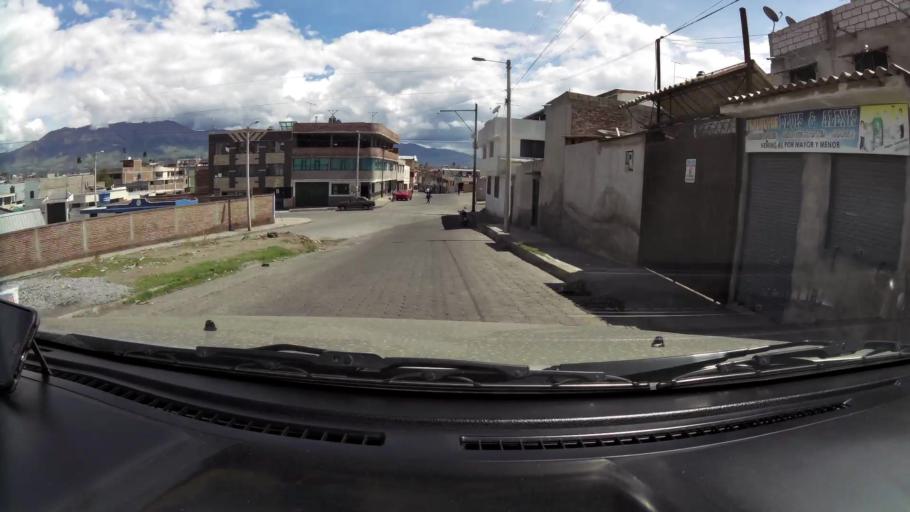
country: EC
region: Chimborazo
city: Riobamba
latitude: -1.6609
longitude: -78.6417
